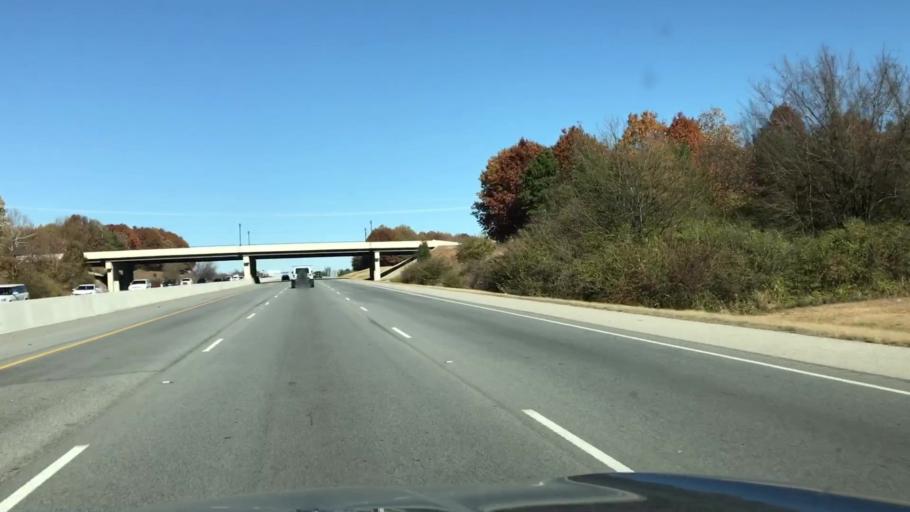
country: US
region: Arkansas
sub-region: Benton County
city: Lowell
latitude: 36.2521
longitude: -94.1503
